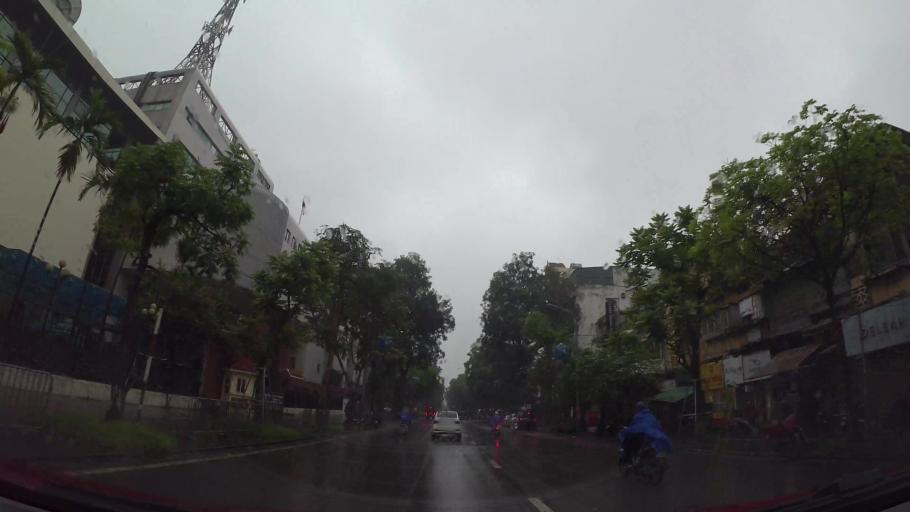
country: VN
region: Ha Noi
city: Hoan Kiem
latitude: 21.0227
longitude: 105.8506
